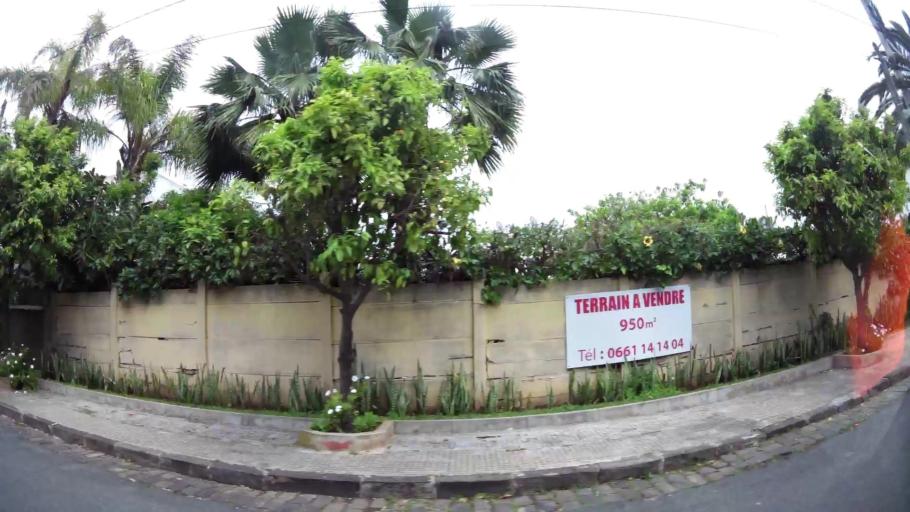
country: MA
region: Grand Casablanca
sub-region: Casablanca
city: Casablanca
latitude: 33.5609
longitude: -7.6367
